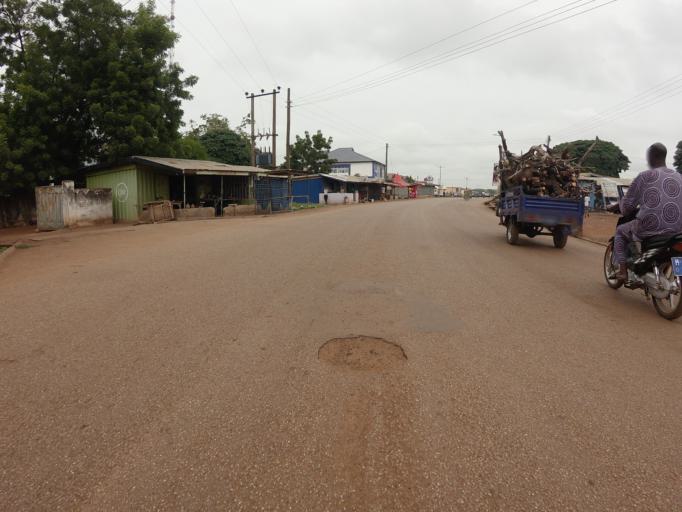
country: GH
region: Northern
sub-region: Yendi
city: Yendi
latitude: 9.4445
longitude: -0.0060
